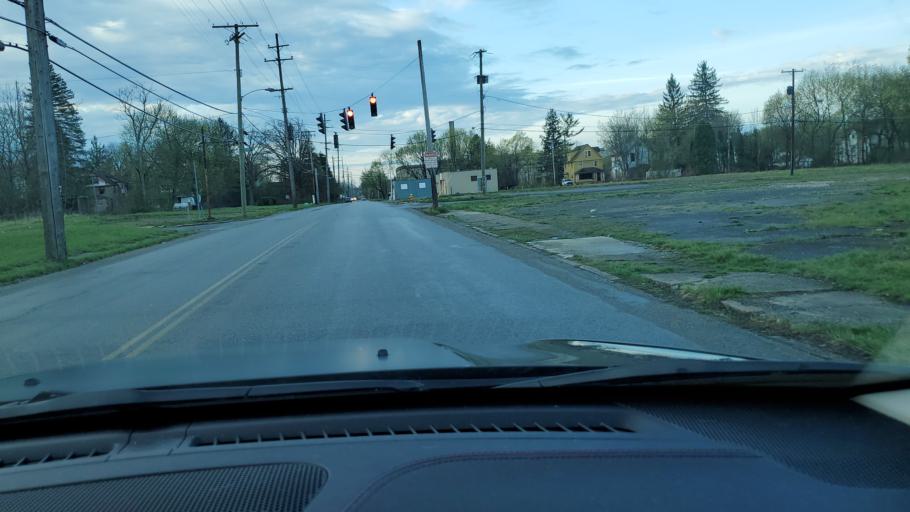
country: US
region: Ohio
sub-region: Mahoning County
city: Youngstown
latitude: 41.0766
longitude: -80.6640
